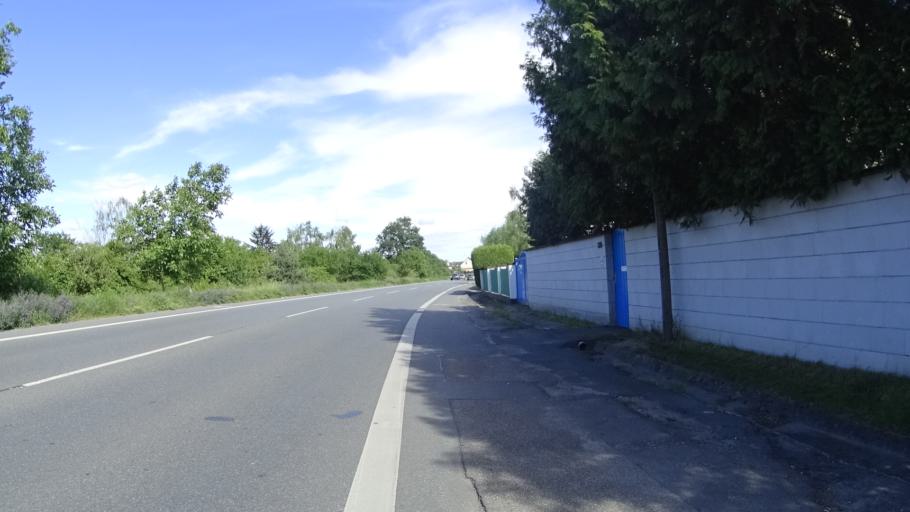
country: DE
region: Hesse
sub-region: Regierungsbezirk Darmstadt
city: Hanau am Main
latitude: 50.1234
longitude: 8.9000
